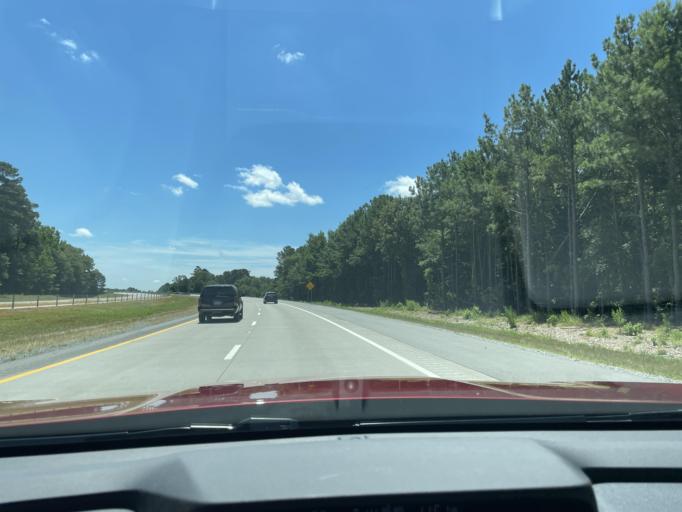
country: US
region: Arkansas
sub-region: Jefferson County
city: Sulphur Springs
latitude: 34.1968
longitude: -92.0692
